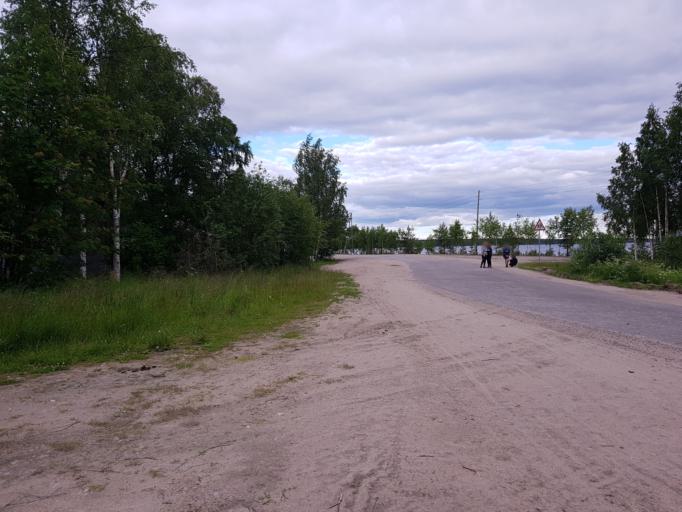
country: RU
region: Republic of Karelia
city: Kalevala
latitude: 65.1938
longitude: 31.1765
